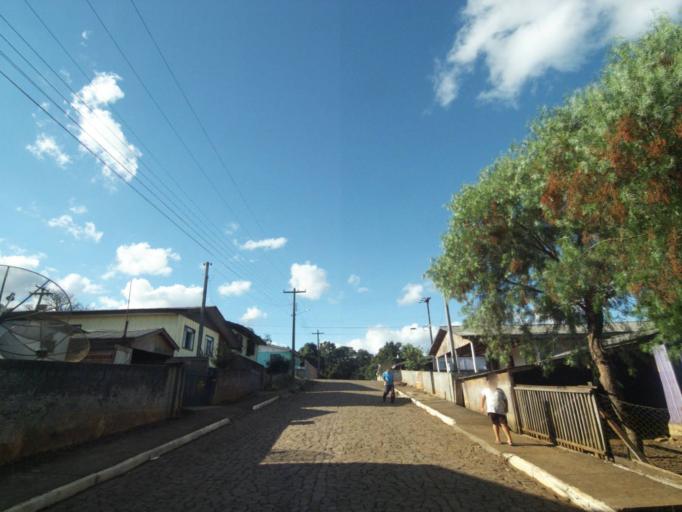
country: BR
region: Parana
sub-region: Uniao Da Vitoria
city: Uniao da Vitoria
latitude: -26.1601
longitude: -51.5337
